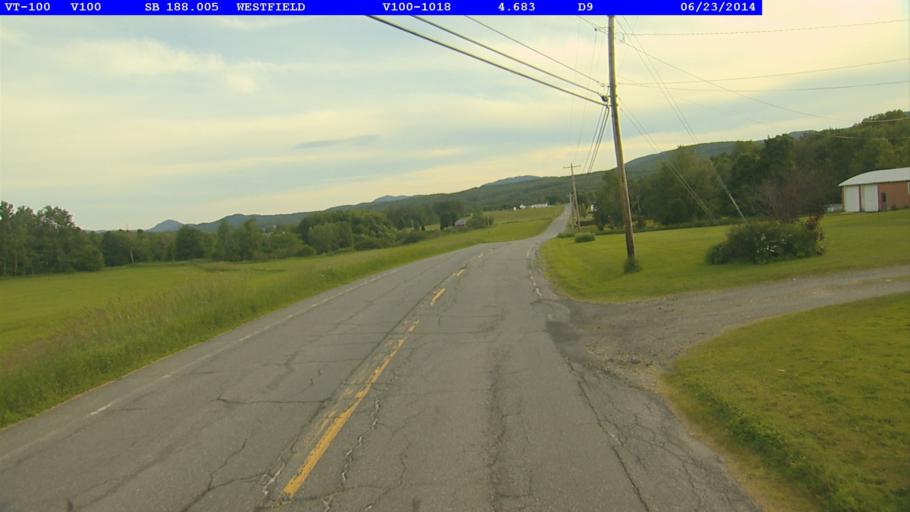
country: US
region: Vermont
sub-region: Orleans County
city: Newport
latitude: 44.8966
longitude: -72.4139
